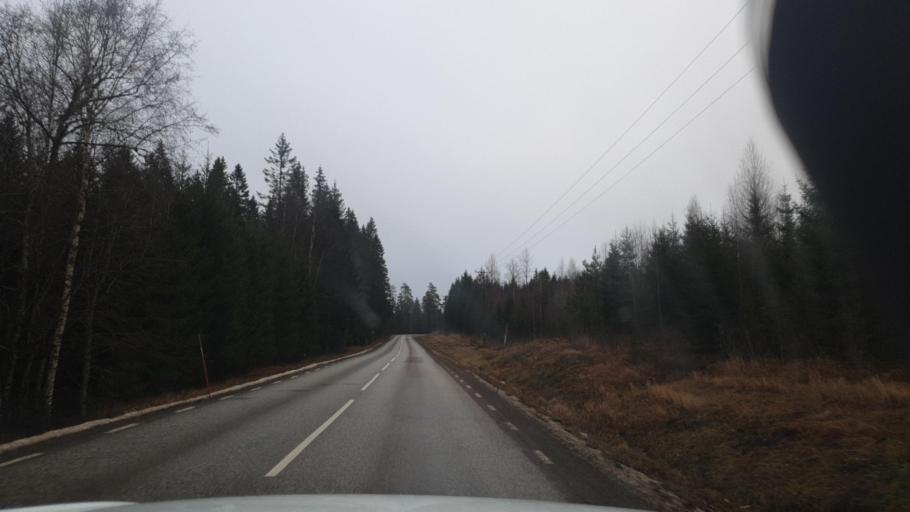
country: SE
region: Vaermland
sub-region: Arjangs Kommun
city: Arjaeng
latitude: 59.5709
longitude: 12.2072
